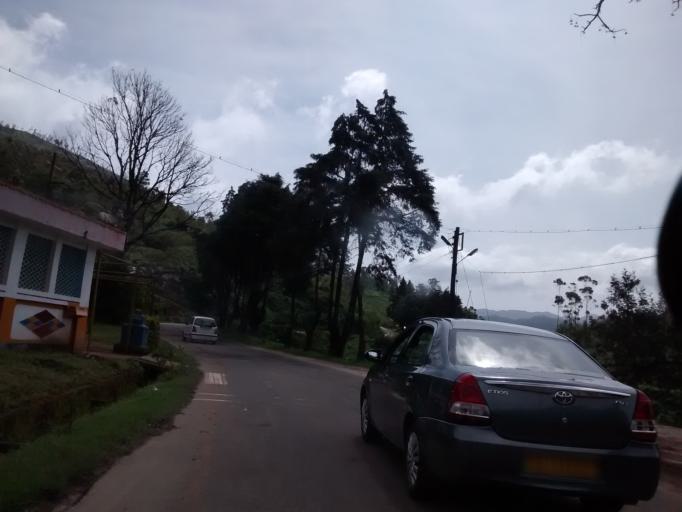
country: IN
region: Kerala
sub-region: Idukki
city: Munnar
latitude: 10.0879
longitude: 77.0821
